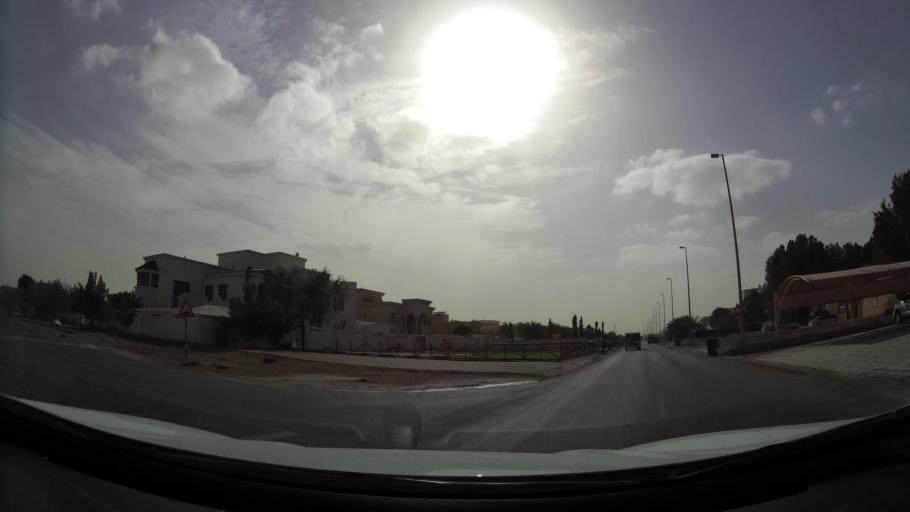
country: AE
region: Abu Dhabi
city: Abu Dhabi
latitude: 24.4116
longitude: 54.6007
